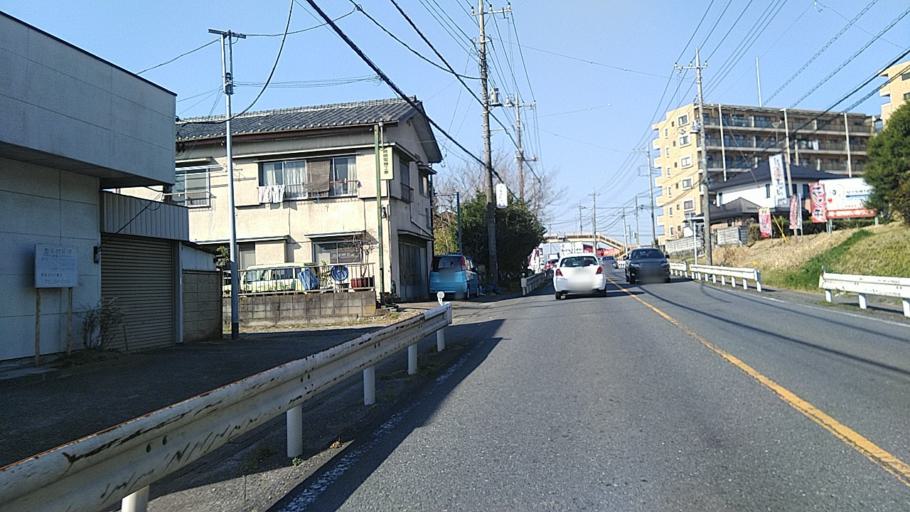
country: JP
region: Saitama
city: Fukiage-fujimi
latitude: 36.0641
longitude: 139.4082
